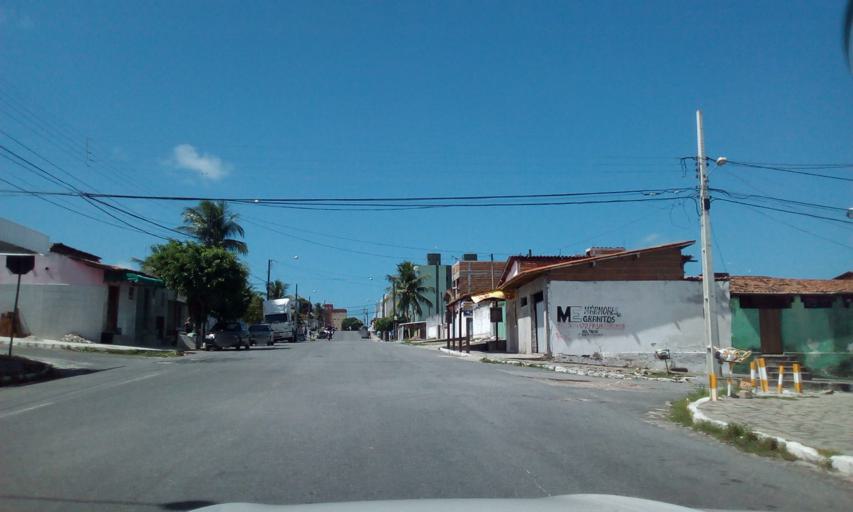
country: BR
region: Paraiba
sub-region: Joao Pessoa
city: Joao Pessoa
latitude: -7.1869
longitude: -34.8462
